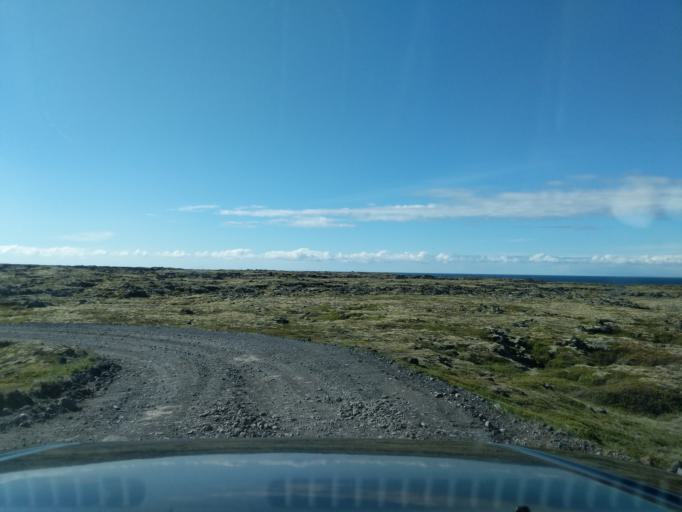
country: IS
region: West
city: Olafsvik
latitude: 64.8741
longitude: -24.0134
